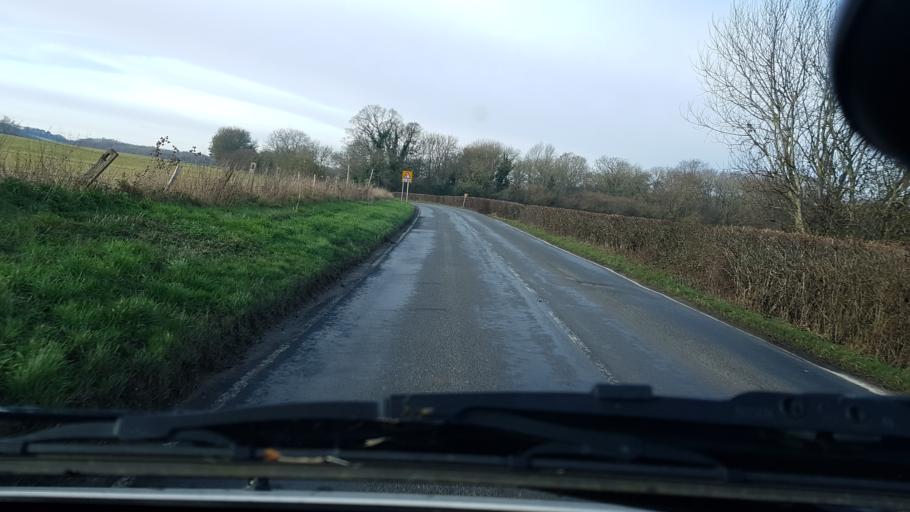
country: GB
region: England
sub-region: Surrey
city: Normandy
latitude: 51.2327
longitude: -0.6664
